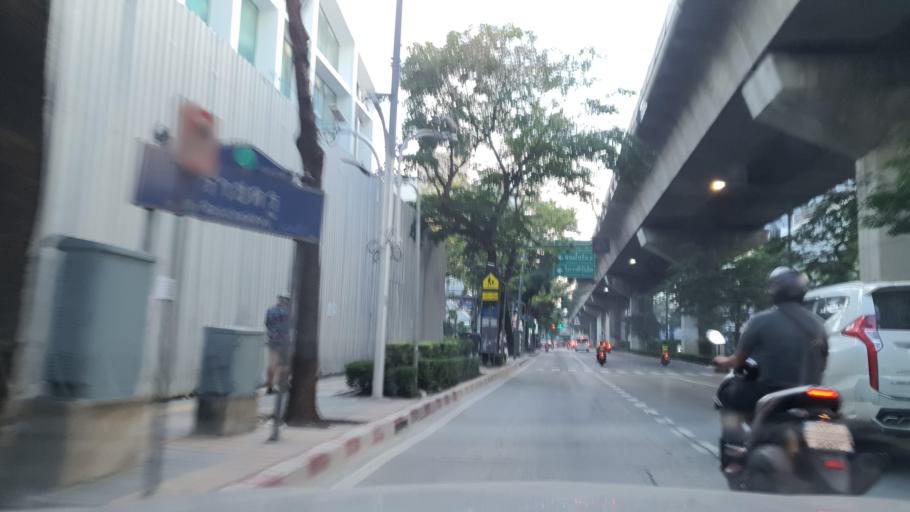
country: TH
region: Bangkok
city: Phaya Thai
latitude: 13.7769
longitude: 100.5444
